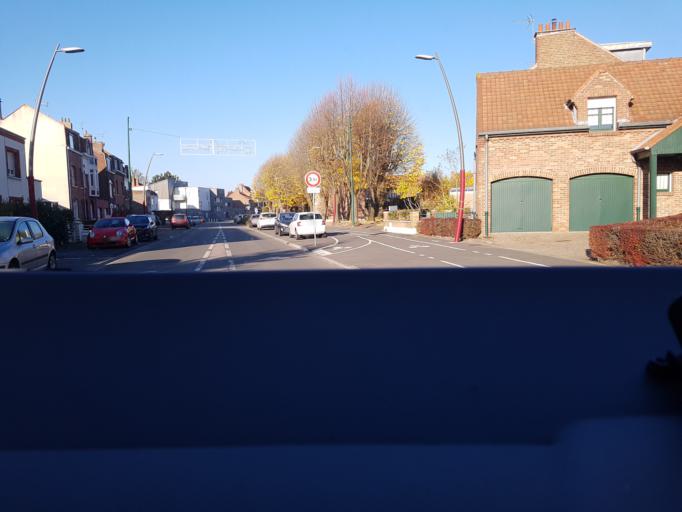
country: FR
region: Nord-Pas-de-Calais
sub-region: Departement du Nord
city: Wambrechies
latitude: 50.6839
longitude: 3.0400
